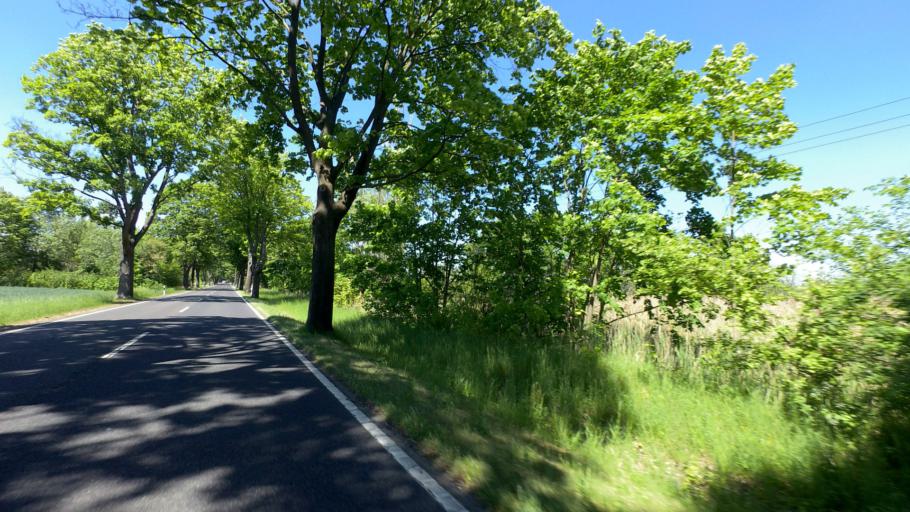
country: DE
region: Brandenburg
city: Lieberose
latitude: 51.9698
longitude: 14.3100
